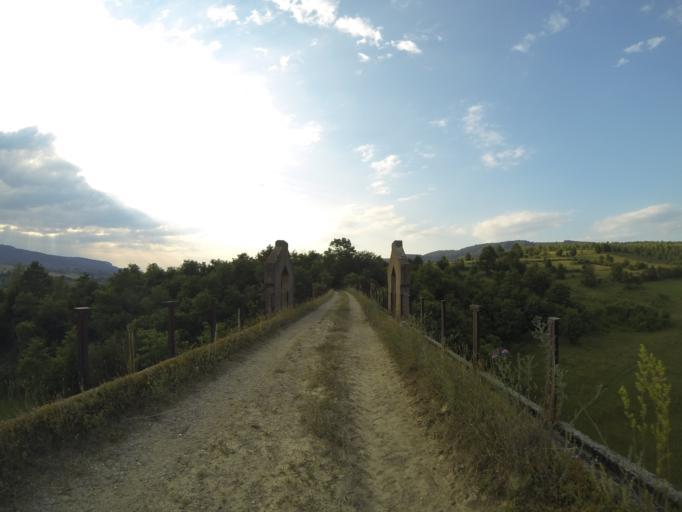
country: RO
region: Brasov
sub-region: Comuna Sinca Noua
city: Sinca Noua
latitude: 45.7166
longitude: 25.2515
